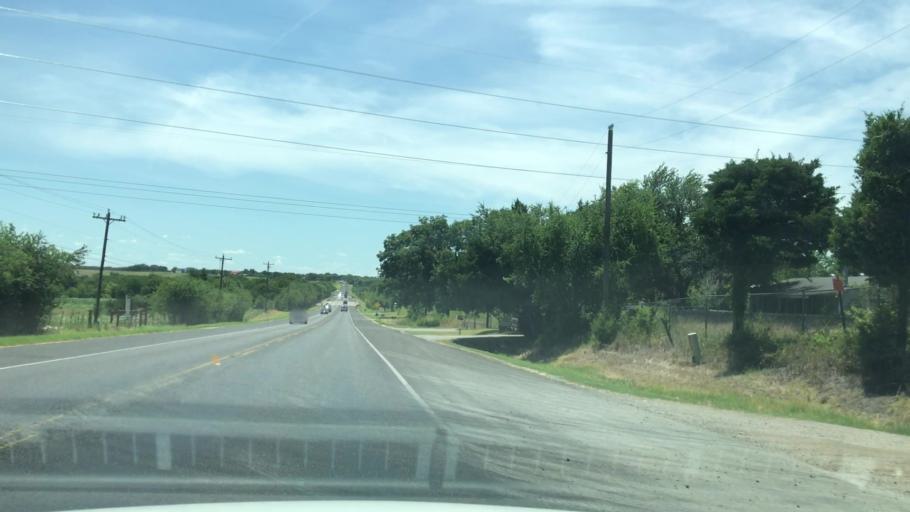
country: US
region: Texas
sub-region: Collin County
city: Lavon
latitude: 32.9891
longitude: -96.4668
